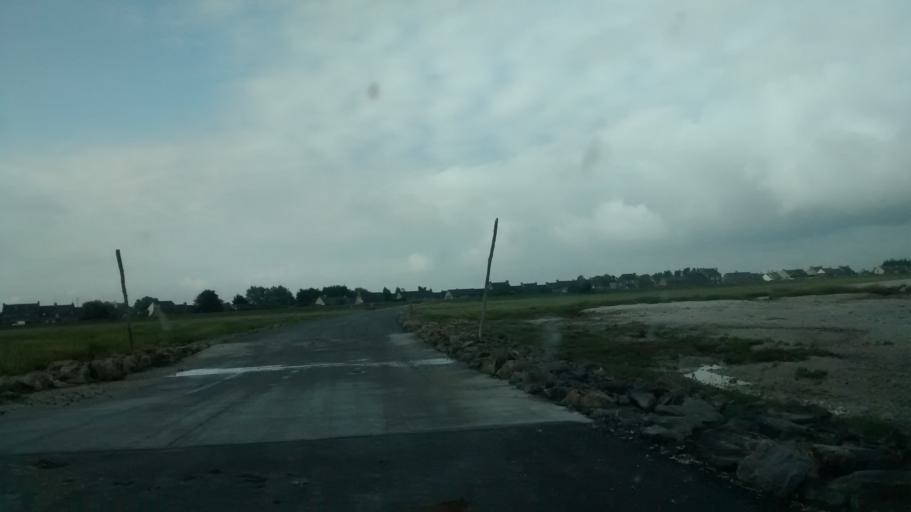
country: FR
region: Brittany
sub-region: Departement d'Ille-et-Vilaine
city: Le Vivier-sur-Mer
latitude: 48.6081
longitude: -1.7460
